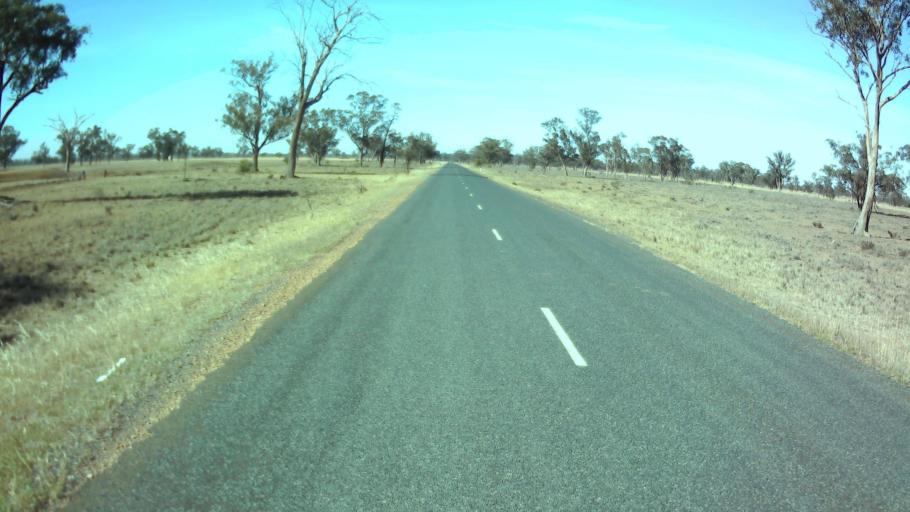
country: AU
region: New South Wales
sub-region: Weddin
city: Grenfell
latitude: -34.0709
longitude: 147.9038
